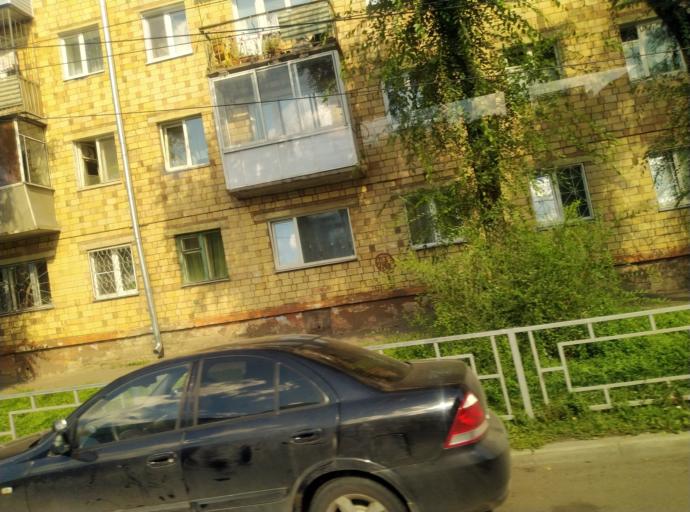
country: RU
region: Krasnoyarskiy
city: Krasnoyarsk
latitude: 55.9772
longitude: 92.8480
